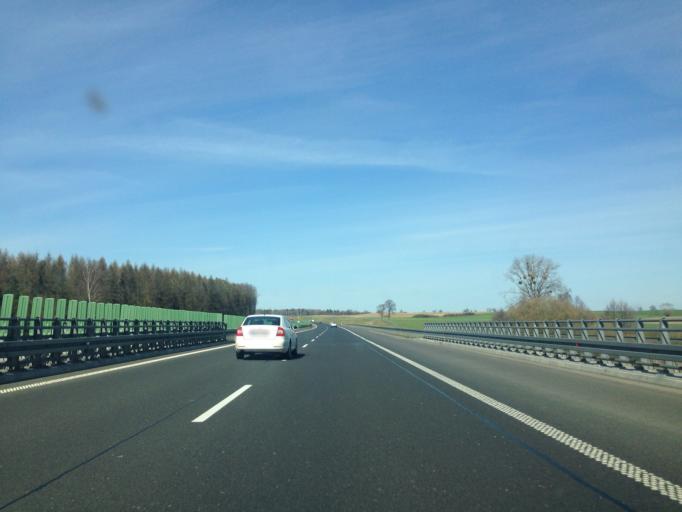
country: PL
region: Pomeranian Voivodeship
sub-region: Powiat starogardzki
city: Smetowo Graniczne
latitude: 53.8147
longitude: 18.6279
